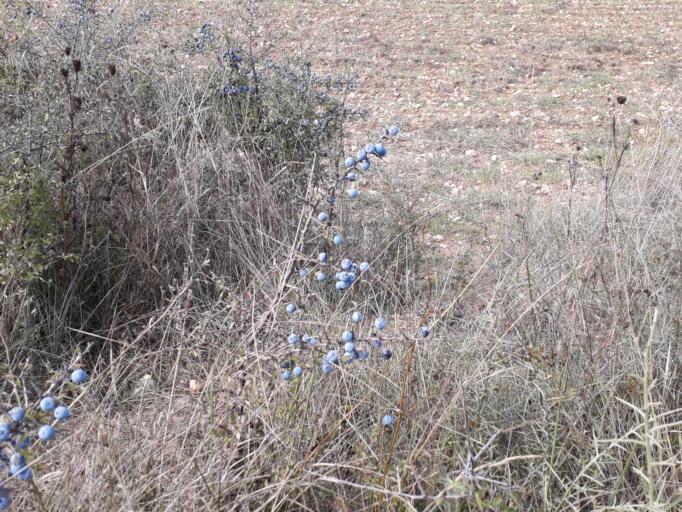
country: ES
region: Catalonia
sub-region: Provincia de Barcelona
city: Bellprat
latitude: 41.4765
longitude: 1.4227
